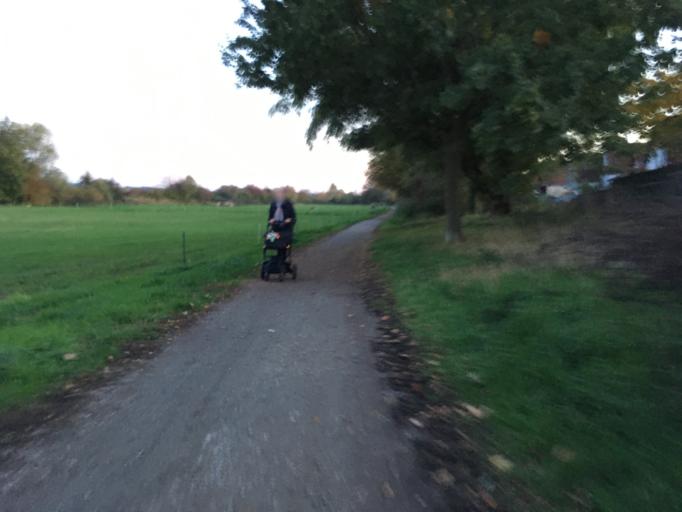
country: DE
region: Hesse
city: Lorsch
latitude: 49.6598
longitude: 8.5705
